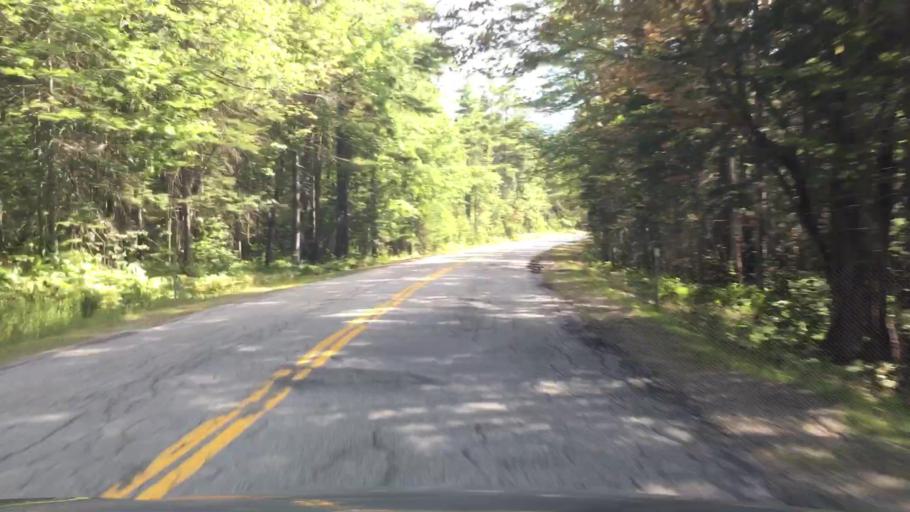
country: US
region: New Hampshire
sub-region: Carroll County
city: Tamworth
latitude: 44.0049
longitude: -71.3206
